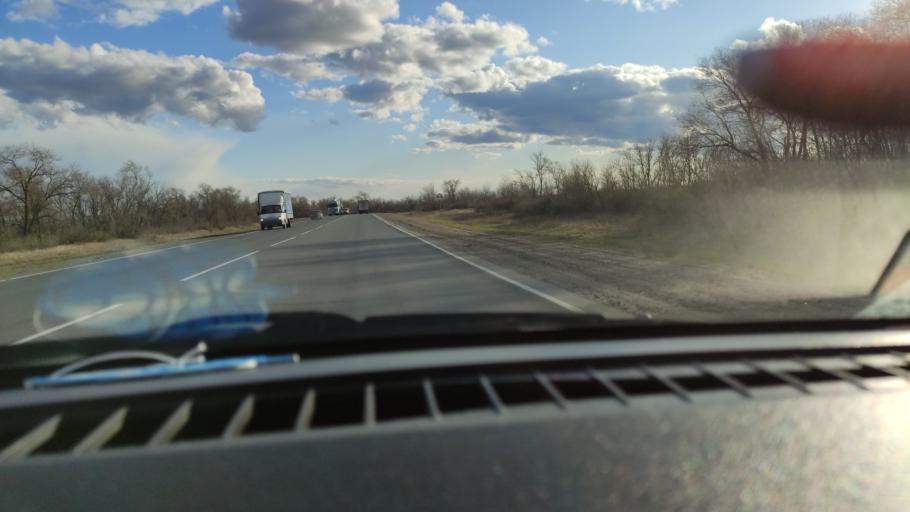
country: RU
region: Saratov
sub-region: Saratovskiy Rayon
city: Saratov
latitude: 51.7059
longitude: 46.0141
